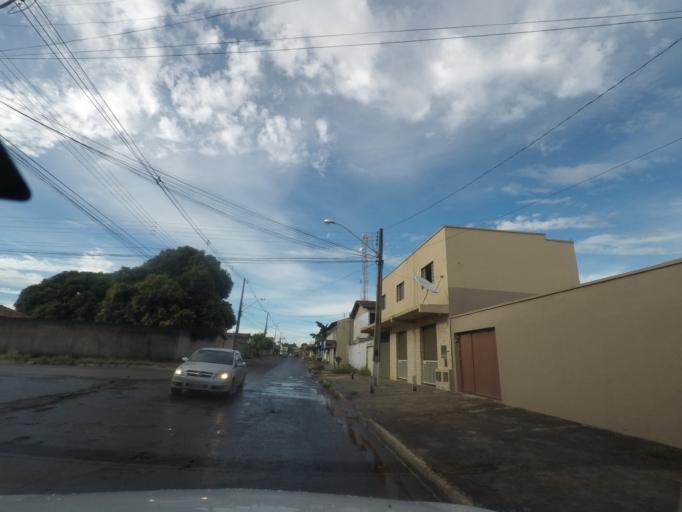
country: BR
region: Goias
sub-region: Aparecida De Goiania
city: Aparecida de Goiania
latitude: -16.7644
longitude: -49.3517
